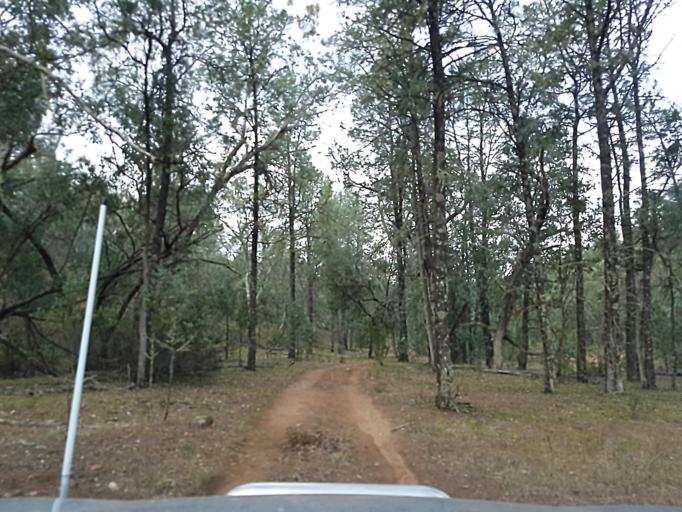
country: AU
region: New South Wales
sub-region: Snowy River
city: Jindabyne
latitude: -36.9472
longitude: 148.3810
